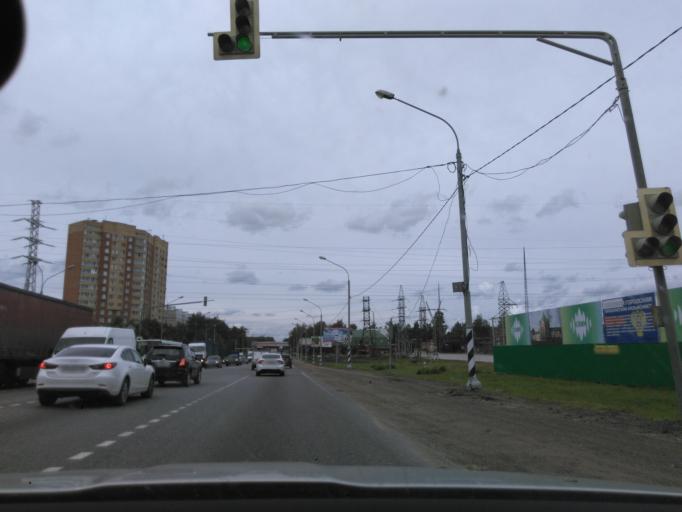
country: RU
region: Moskovskaya
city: Klin
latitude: 56.3217
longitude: 36.7606
